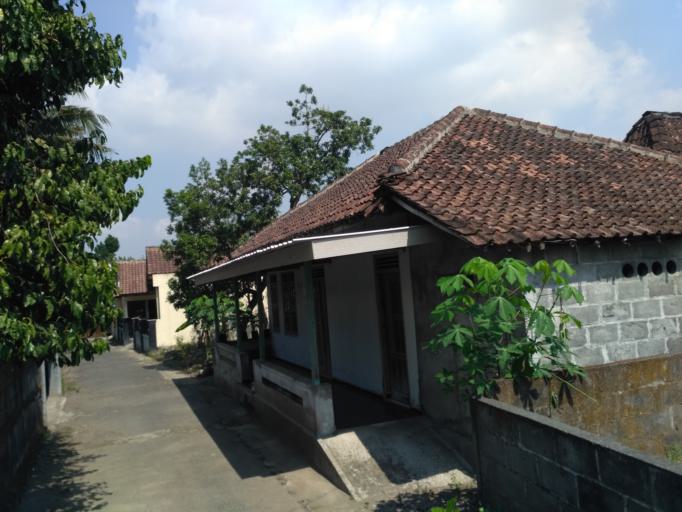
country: ID
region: Daerah Istimewa Yogyakarta
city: Depok
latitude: -7.7088
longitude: 110.4171
